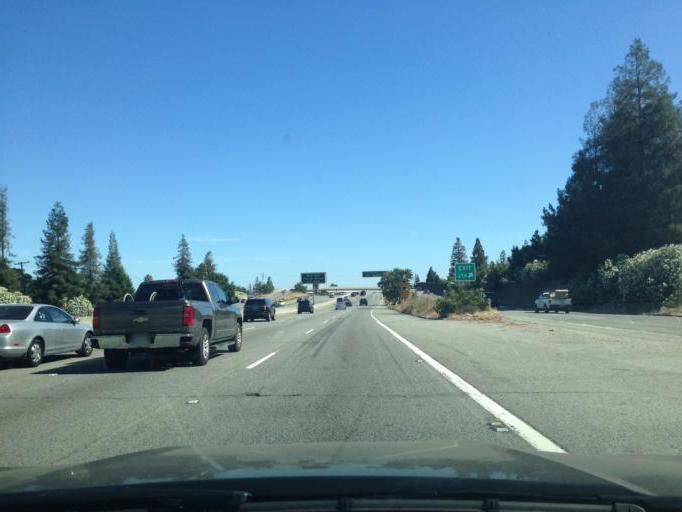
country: US
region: California
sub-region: Santa Clara County
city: Burbank
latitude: 37.3123
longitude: -121.9405
